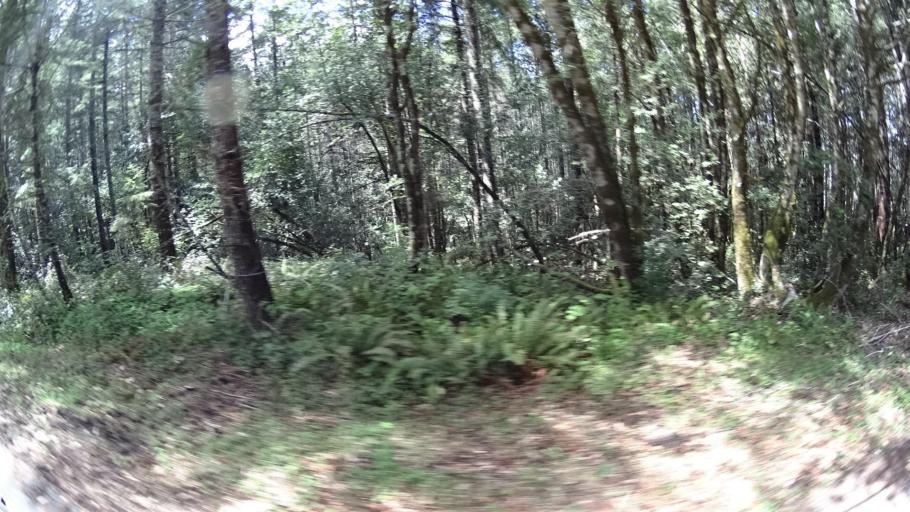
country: US
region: California
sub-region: Humboldt County
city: Blue Lake
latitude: 40.7612
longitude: -123.9626
